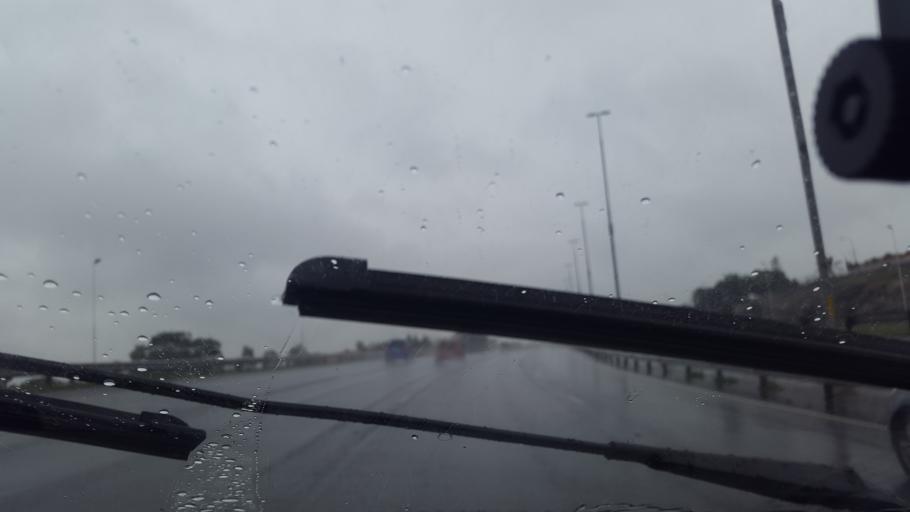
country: ZA
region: Gauteng
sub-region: City of Johannesburg Metropolitan Municipality
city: Johannesburg
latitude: -26.2613
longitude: 28.0061
